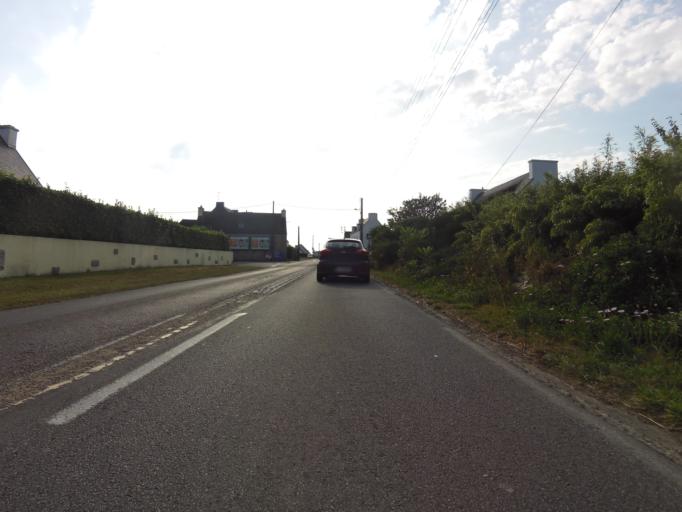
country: FR
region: Brittany
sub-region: Departement du Finistere
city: Plozevet
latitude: 47.9855
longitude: -4.4127
